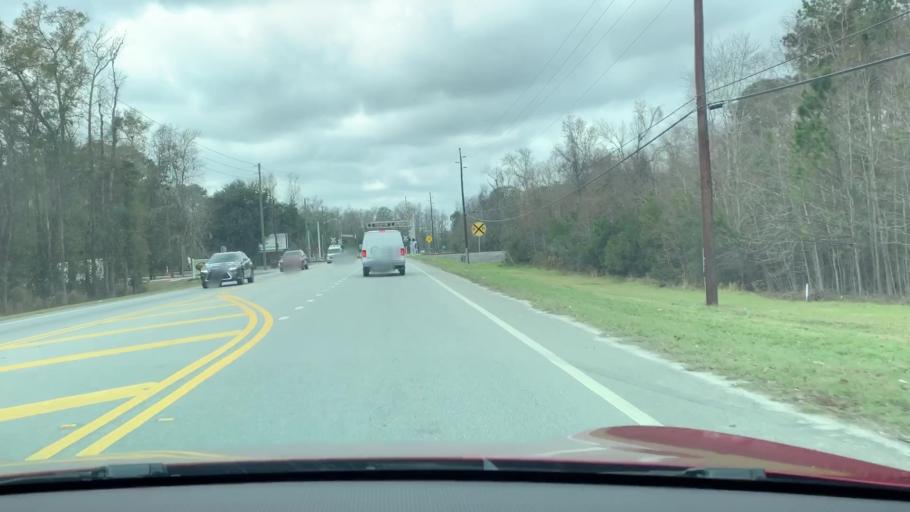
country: US
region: Georgia
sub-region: Chatham County
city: Port Wentworth
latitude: 32.1429
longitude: -81.1899
